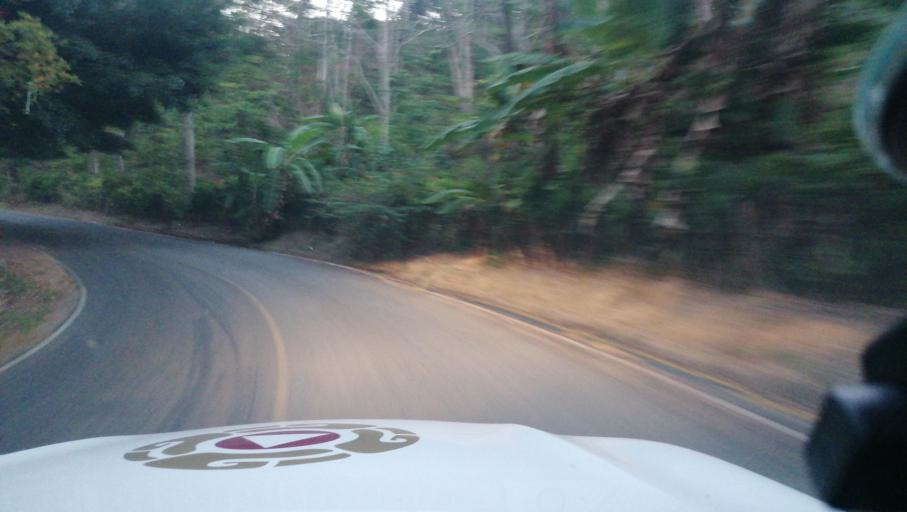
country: MX
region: Chiapas
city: Veinte de Noviembre
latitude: 15.0043
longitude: -92.2451
